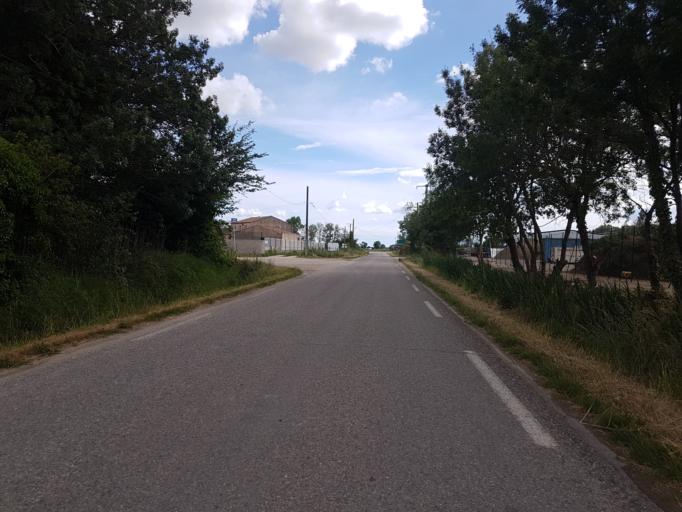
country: FR
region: Languedoc-Roussillon
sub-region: Departement du Gard
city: Saint-Gilles
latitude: 43.6699
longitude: 4.4501
